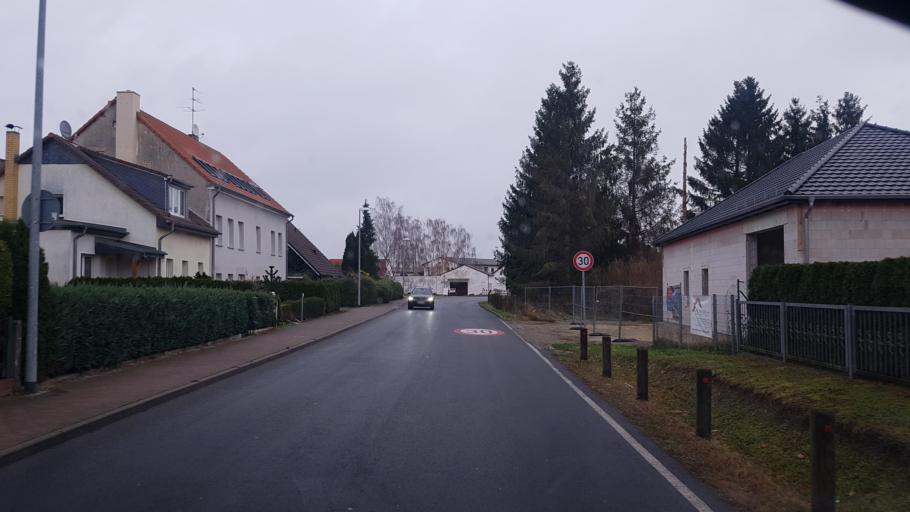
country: DE
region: Brandenburg
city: Brandenburg an der Havel
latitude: 52.4353
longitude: 12.6248
